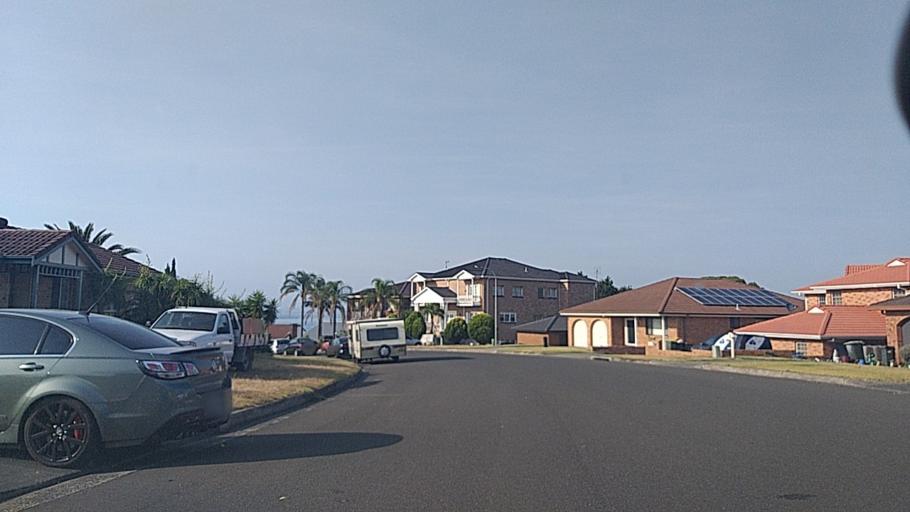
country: AU
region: New South Wales
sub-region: Wollongong
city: Berkeley
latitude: -34.4777
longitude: 150.8587
